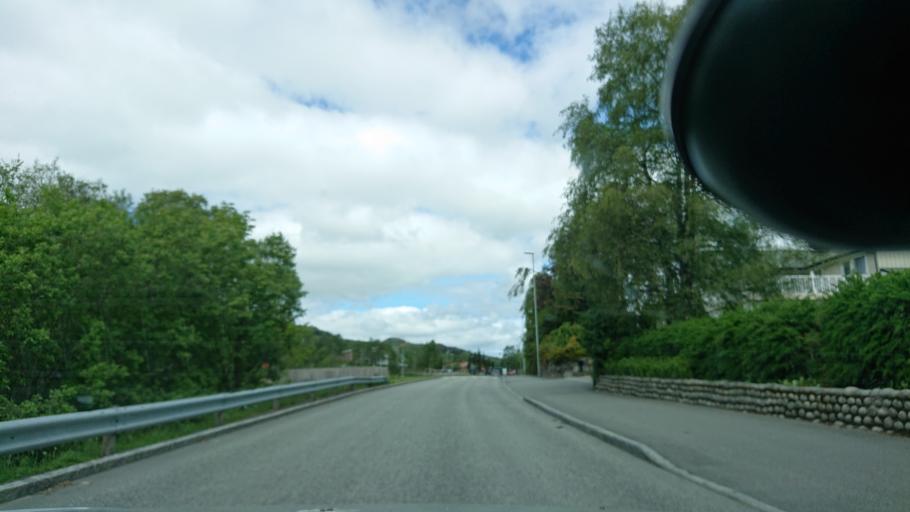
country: NO
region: Rogaland
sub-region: Gjesdal
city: Algard
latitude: 58.7702
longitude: 5.8652
